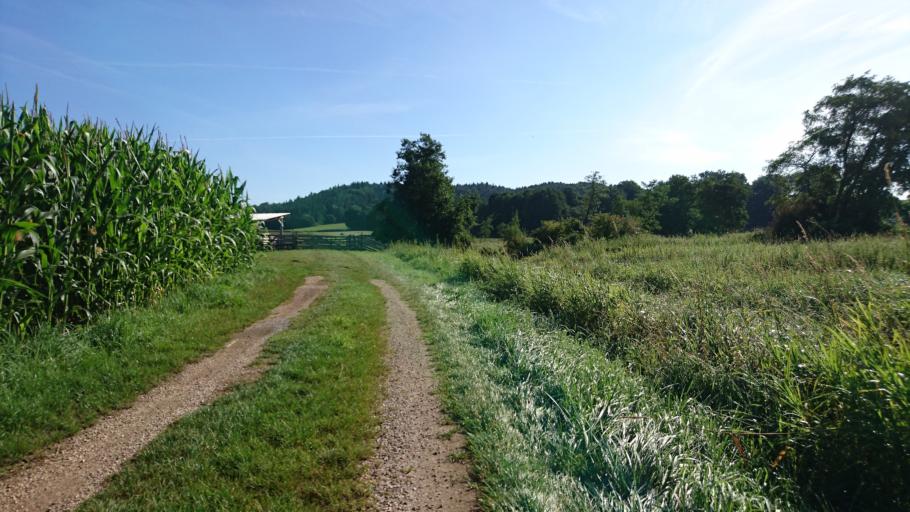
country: DE
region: Bavaria
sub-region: Swabia
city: Altenmunster
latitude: 48.4438
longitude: 10.5975
